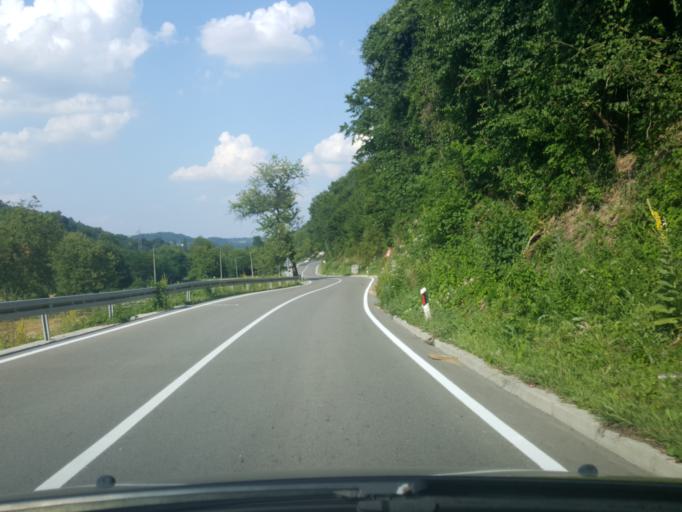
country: RS
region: Central Serbia
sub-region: Sumadijski Okrug
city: Arangelovac
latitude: 44.1700
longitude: 20.5175
